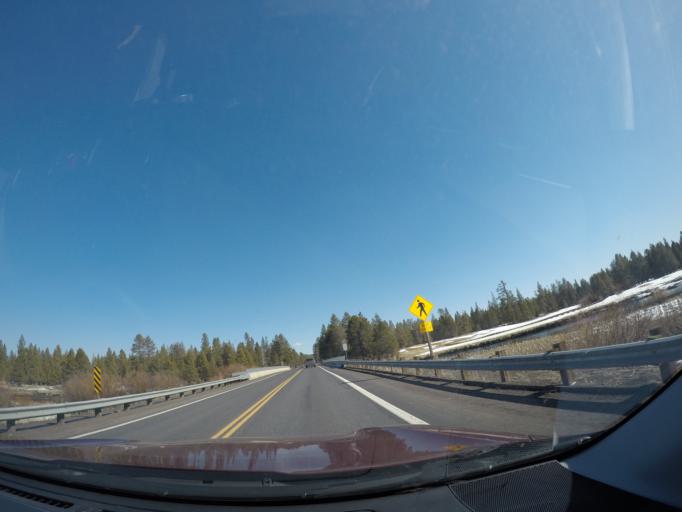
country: US
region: Oregon
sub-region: Deschutes County
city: Sunriver
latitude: 43.8631
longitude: -121.4530
